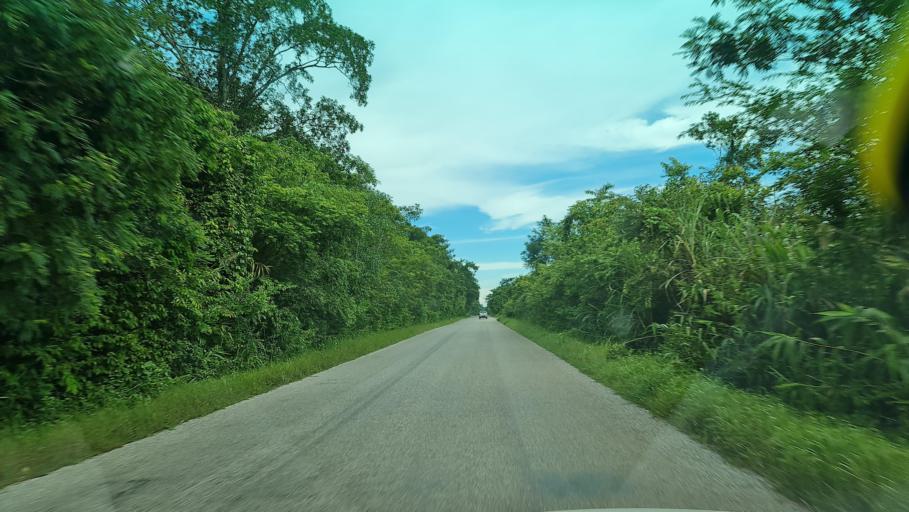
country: TH
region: Nakhon Phanom
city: Ban Phaeng
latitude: 17.9655
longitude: 104.3290
